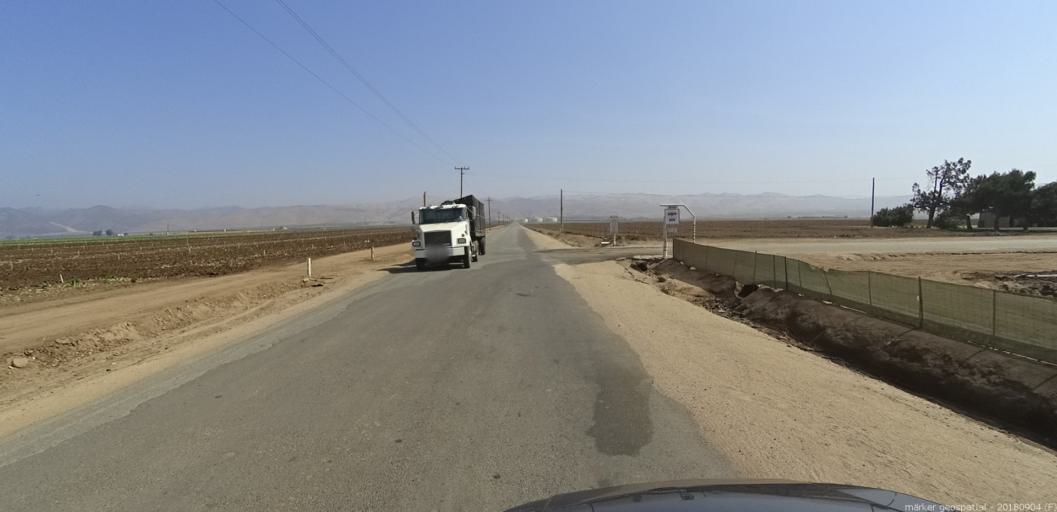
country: US
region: California
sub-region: Monterey County
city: Gonzales
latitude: 36.5172
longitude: -121.4308
